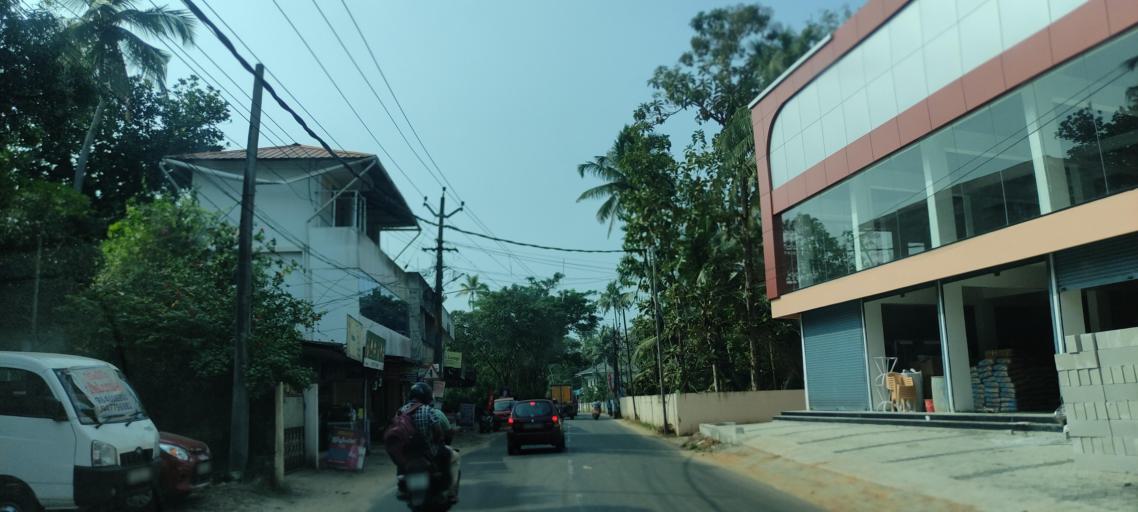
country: IN
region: Kerala
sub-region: Alappuzha
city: Vayalar
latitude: 9.6928
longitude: 76.3343
